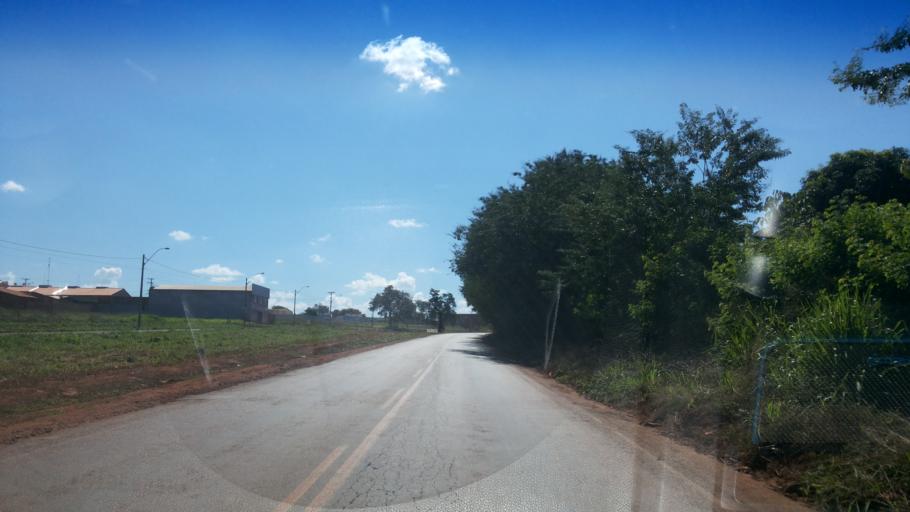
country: BR
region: Goias
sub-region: Goiania
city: Goiania
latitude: -16.5604
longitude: -49.2680
